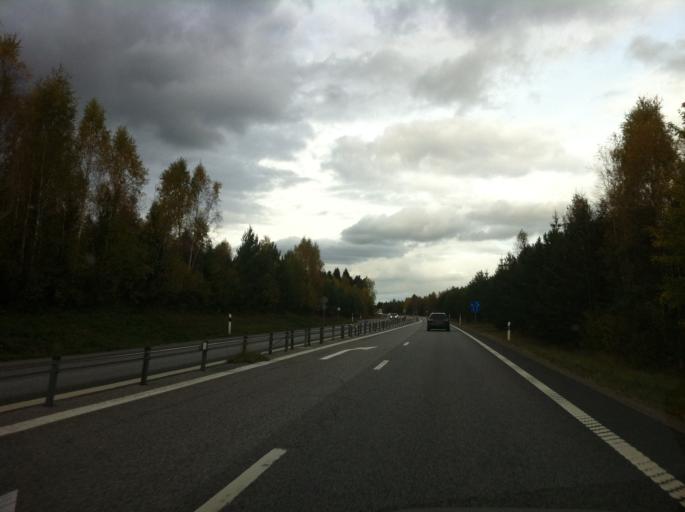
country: SE
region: OEstergoetland
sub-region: Motala Kommun
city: Motala
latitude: 58.5902
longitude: 14.9884
